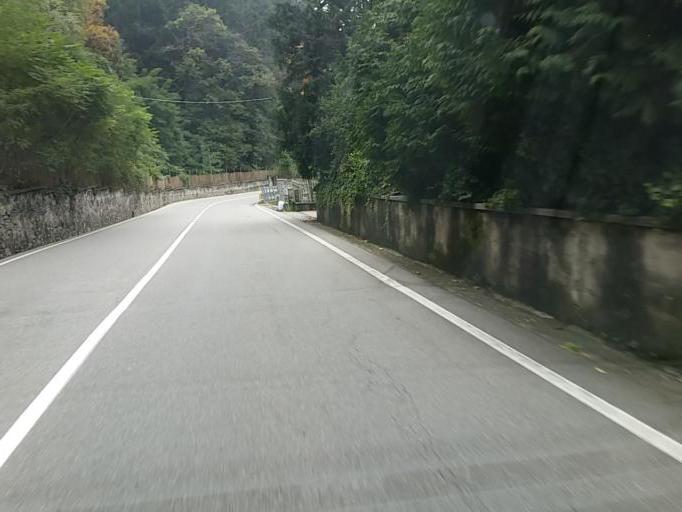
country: IT
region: Piedmont
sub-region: Provincia di Novara
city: Orta San Giulio
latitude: 45.7943
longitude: 8.4171
